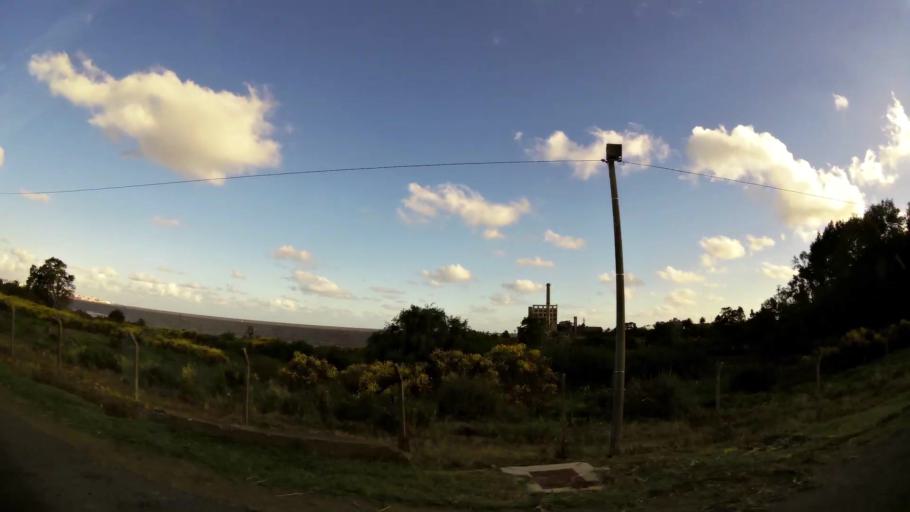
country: UY
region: Montevideo
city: Montevideo
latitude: -34.8984
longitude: -56.2594
